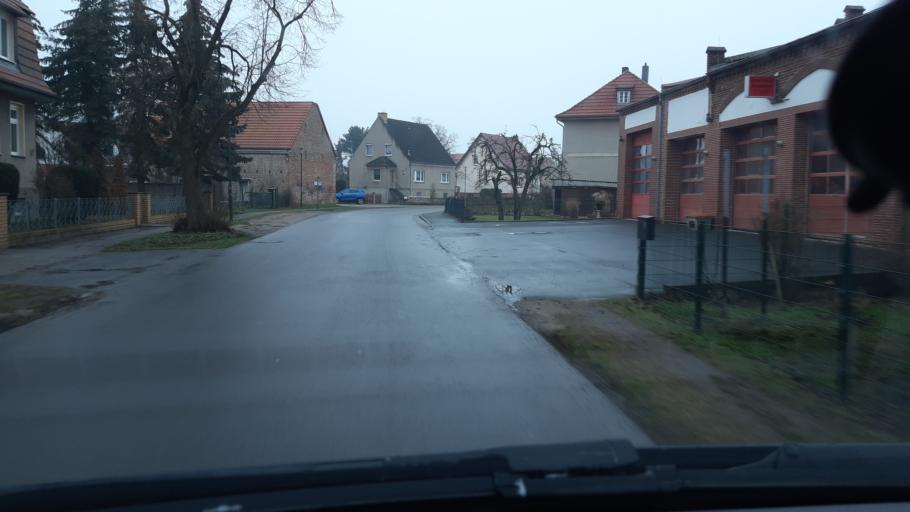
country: DE
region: Brandenburg
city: Kremmen
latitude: 52.7628
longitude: 13.0306
